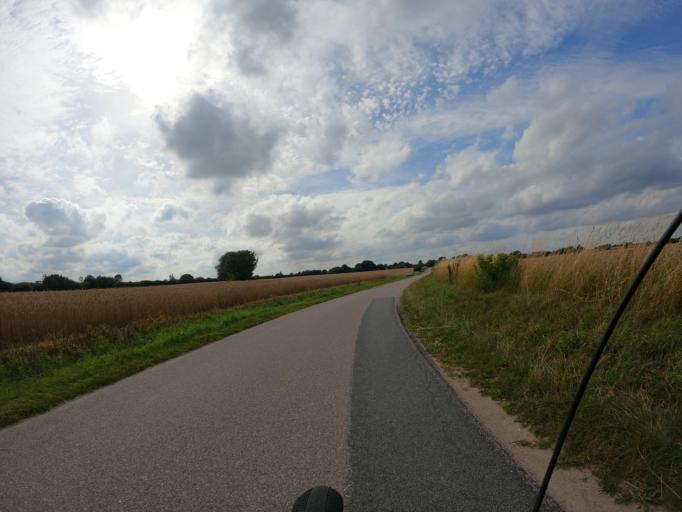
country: DE
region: Schleswig-Holstein
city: Steinberg
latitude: 54.7680
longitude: 9.7753
